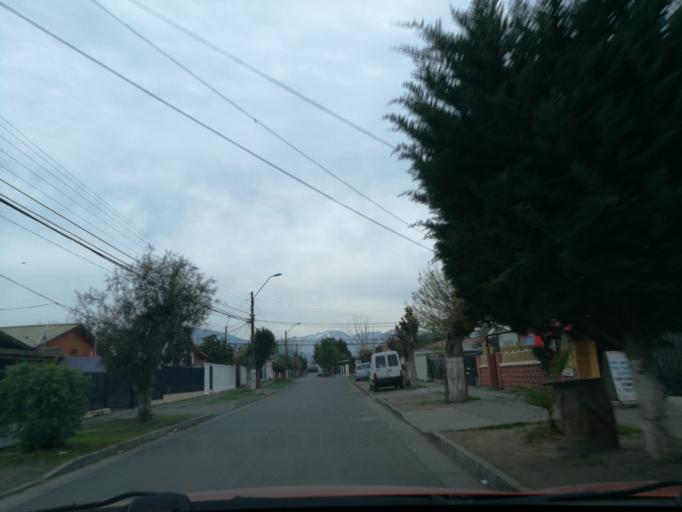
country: CL
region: O'Higgins
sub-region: Provincia de Cachapoal
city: Machali
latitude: -34.1761
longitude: -70.6906
